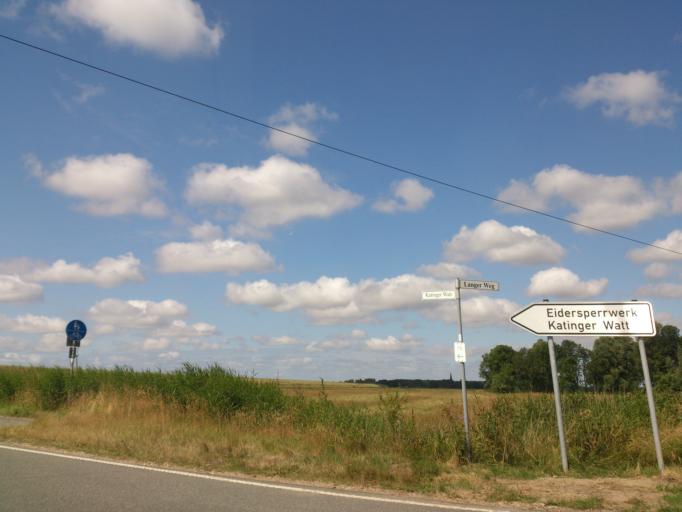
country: DE
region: Schleswig-Holstein
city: Kotzenbull
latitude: 54.3040
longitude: 8.8992
